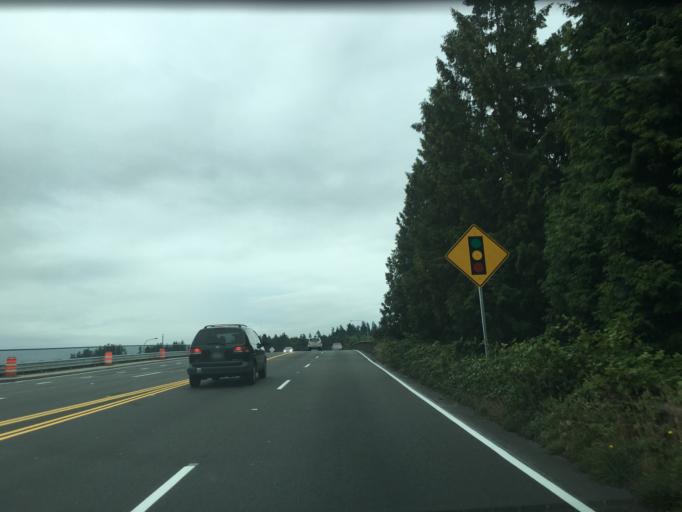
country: US
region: Washington
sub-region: King County
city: Kingsgate
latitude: 47.7106
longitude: -122.1840
